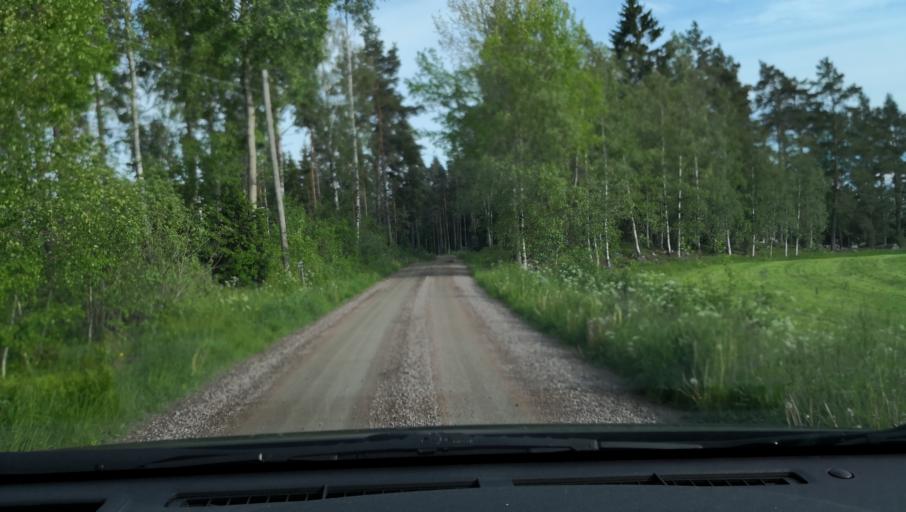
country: SE
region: Vaestmanland
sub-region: Kungsors Kommun
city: Kungsoer
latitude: 59.3601
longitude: 16.0543
